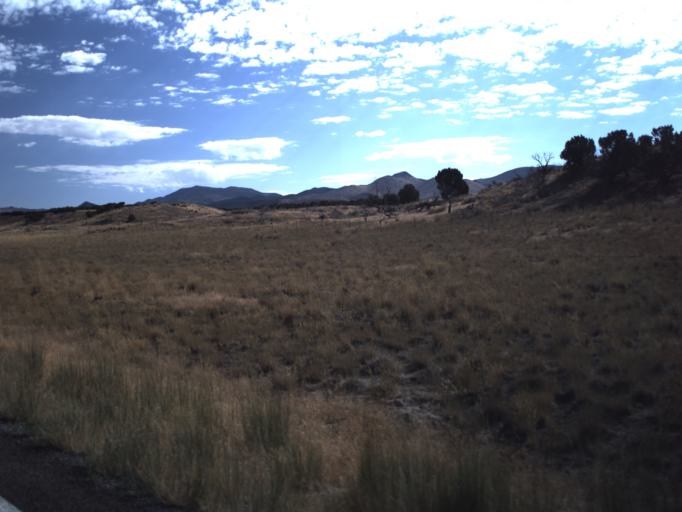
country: US
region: Utah
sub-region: Juab County
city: Mona
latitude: 39.7439
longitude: -112.1870
